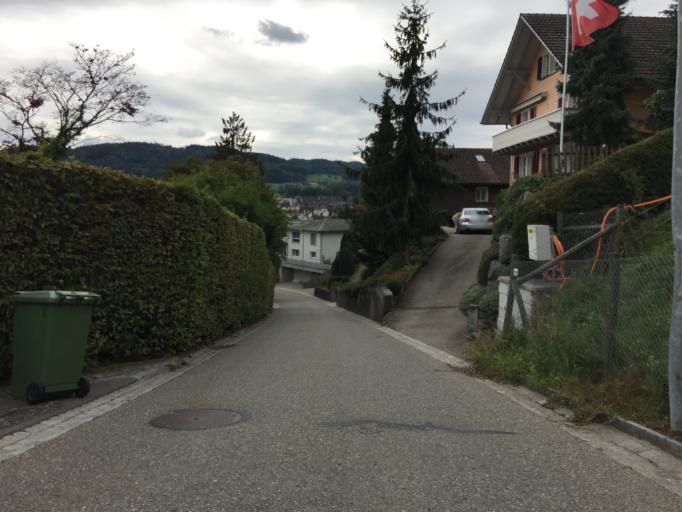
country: CH
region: Saint Gallen
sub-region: Wahlkreis Wil
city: Oberuzwil
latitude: 47.4349
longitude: 9.1275
